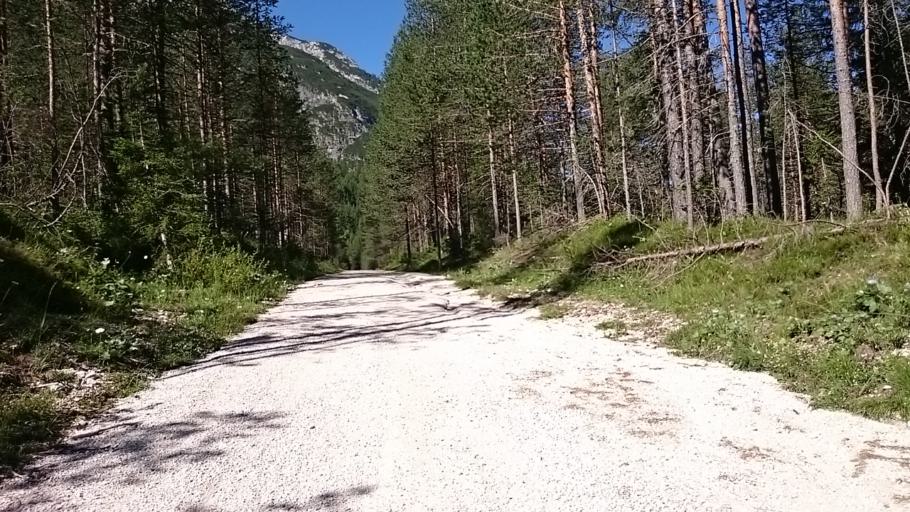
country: IT
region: Trentino-Alto Adige
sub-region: Bolzano
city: Dobbiaco
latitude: 46.6176
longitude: 12.2191
